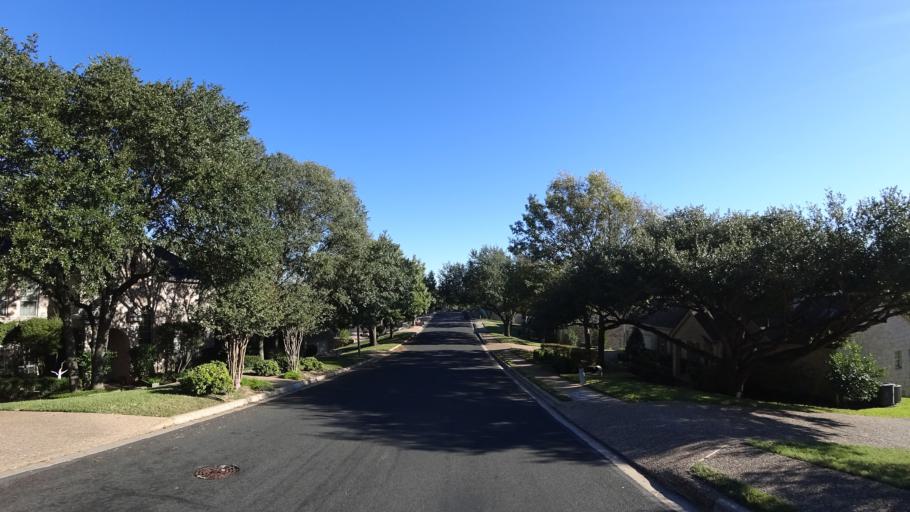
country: US
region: Texas
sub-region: Travis County
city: West Lake Hills
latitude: 30.3295
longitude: -97.8047
